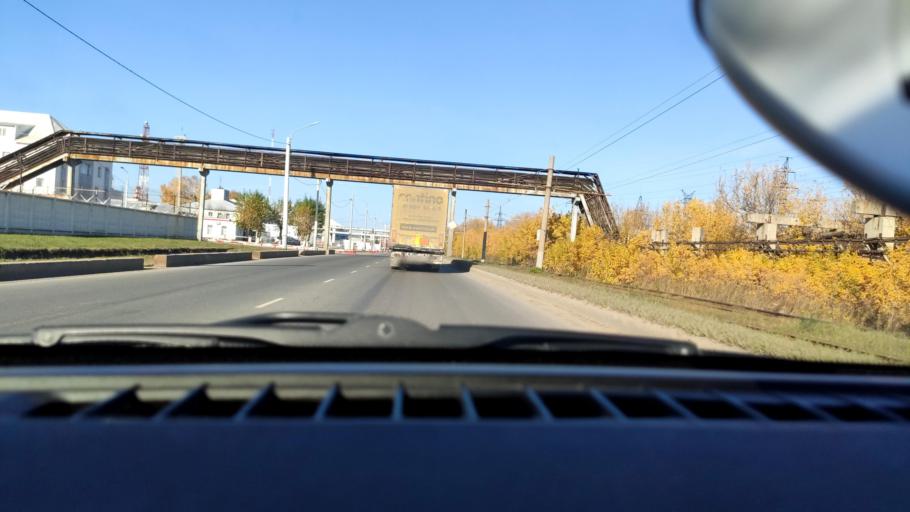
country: RU
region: Perm
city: Gamovo
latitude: 57.9205
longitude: 56.1449
